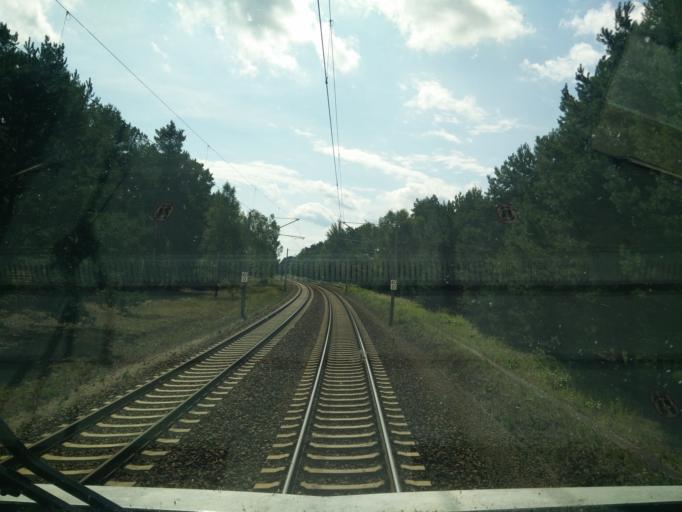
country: DE
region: Brandenburg
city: Schwerin
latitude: 52.1903
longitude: 13.6266
